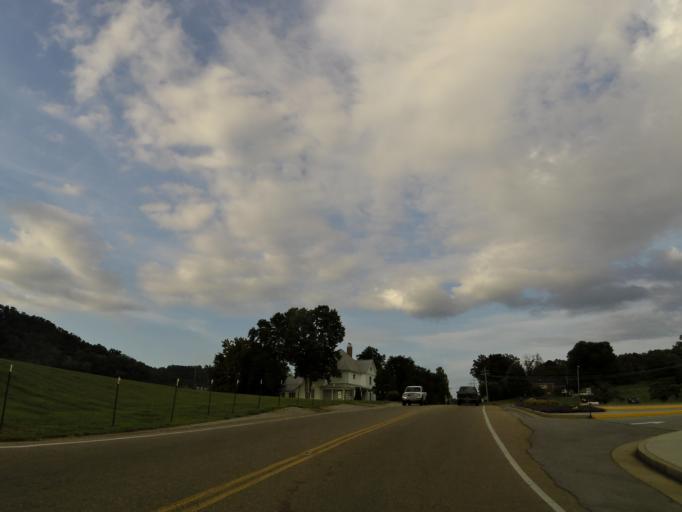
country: US
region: Tennessee
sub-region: Jefferson County
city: Dandridge
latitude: 35.9301
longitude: -83.3400
